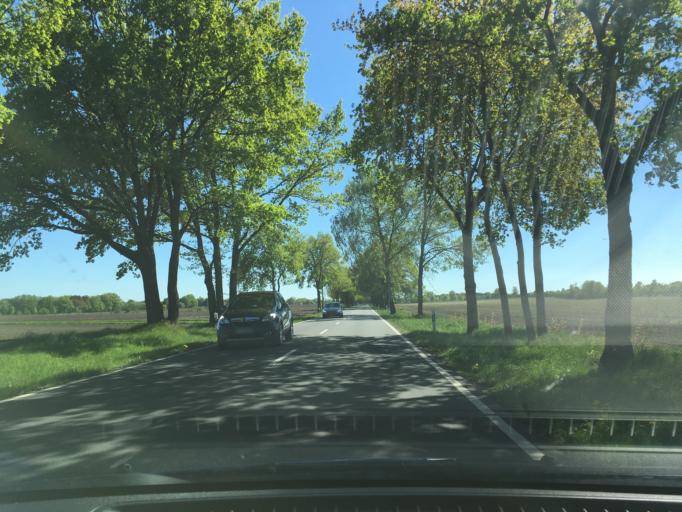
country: DE
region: Lower Saxony
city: Fassberg
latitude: 52.8912
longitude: 10.1171
